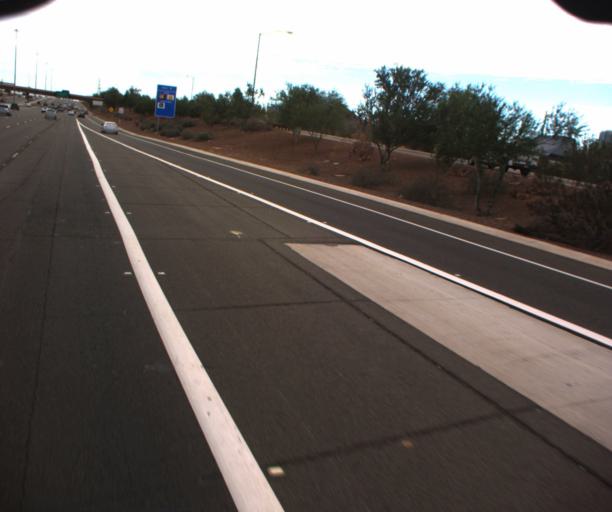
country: US
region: Arizona
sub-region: Maricopa County
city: Tempe Junction
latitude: 33.4361
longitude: -111.9535
